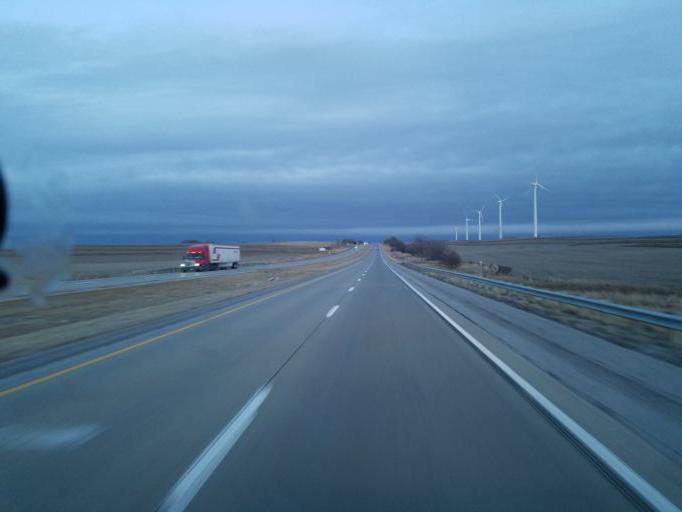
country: US
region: Iowa
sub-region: Pottawattamie County
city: Avoca
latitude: 41.4974
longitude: -95.1920
